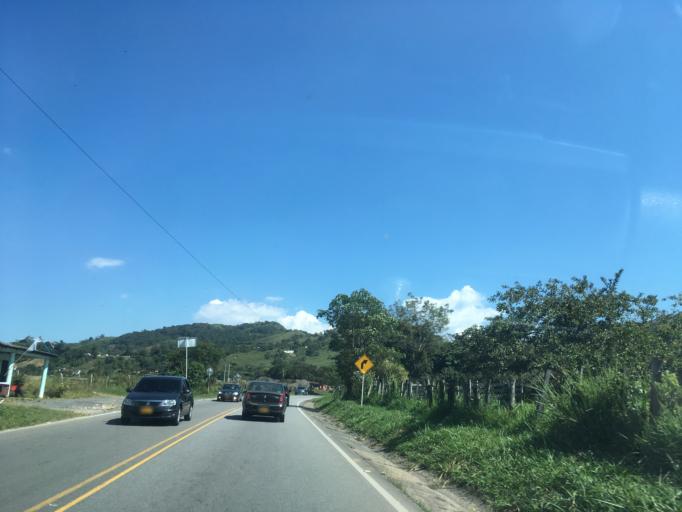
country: CO
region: Santander
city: Suaita
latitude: 6.0666
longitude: -73.4217
